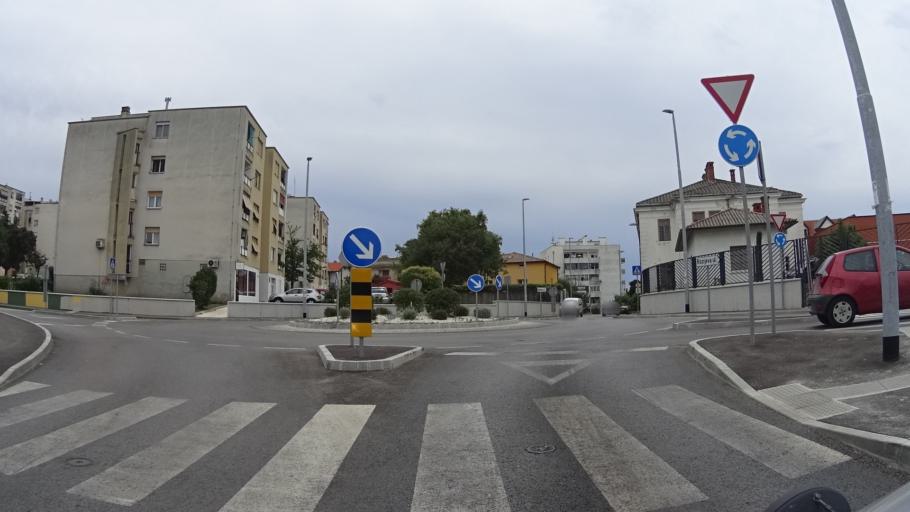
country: HR
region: Istarska
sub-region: Grad Pula
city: Pula
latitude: 44.8583
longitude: 13.8447
